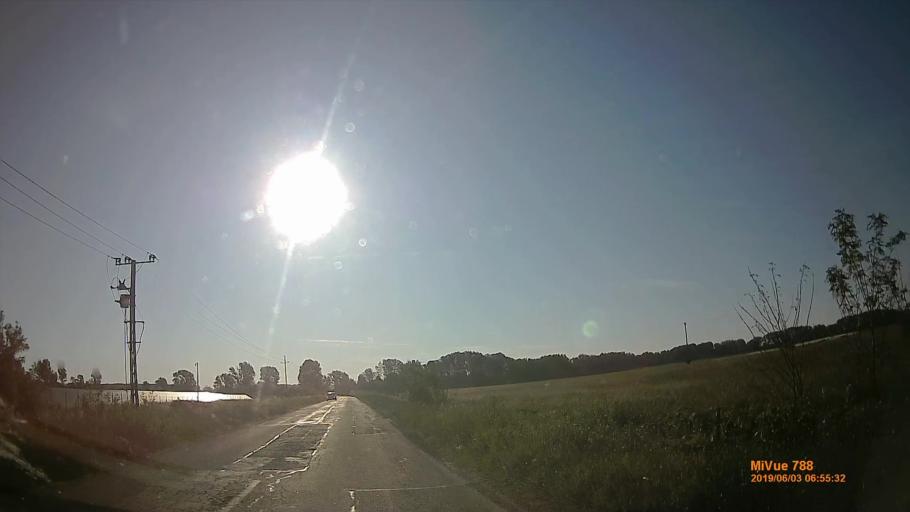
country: HU
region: Pest
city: Dabas
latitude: 47.2166
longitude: 19.2454
